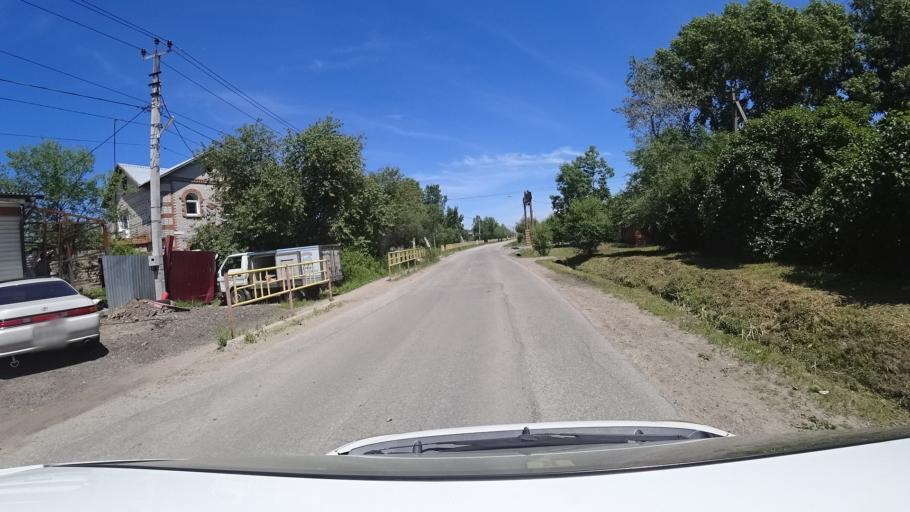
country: RU
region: Khabarovsk Krai
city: Topolevo
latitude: 48.5078
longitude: 135.1824
